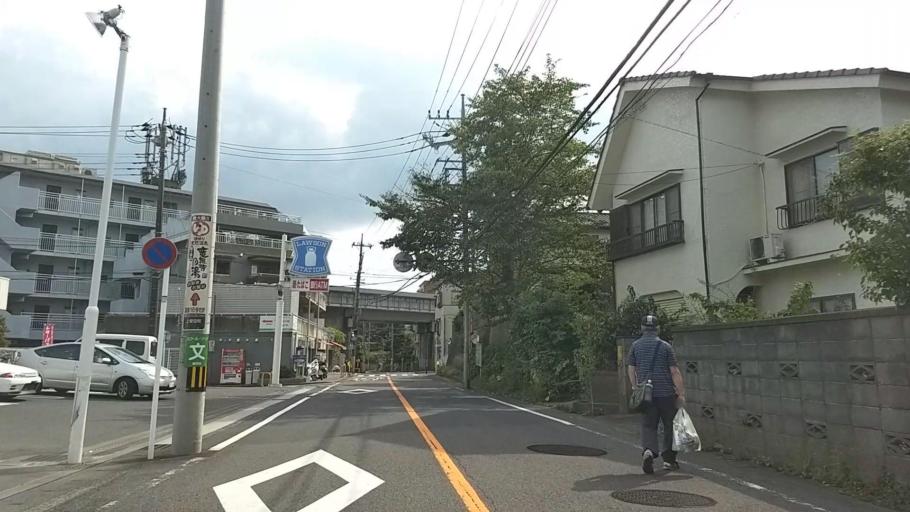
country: JP
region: Kanagawa
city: Yokohama
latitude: 35.4812
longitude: 139.5705
